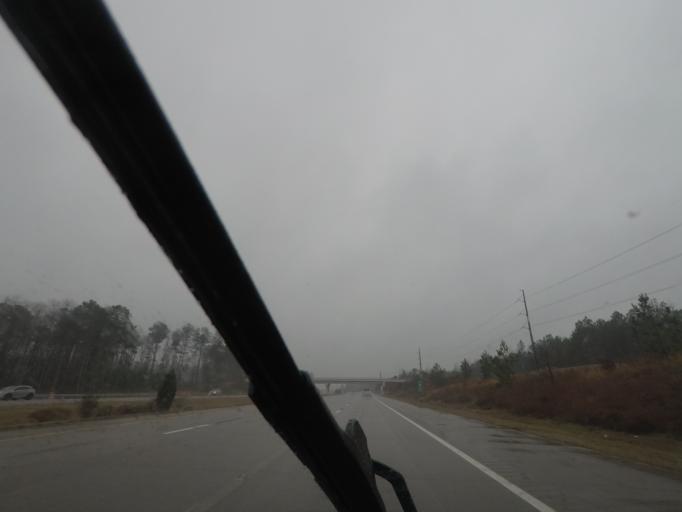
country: US
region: North Carolina
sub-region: Wake County
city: Green Level
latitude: 35.8110
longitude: -78.8925
